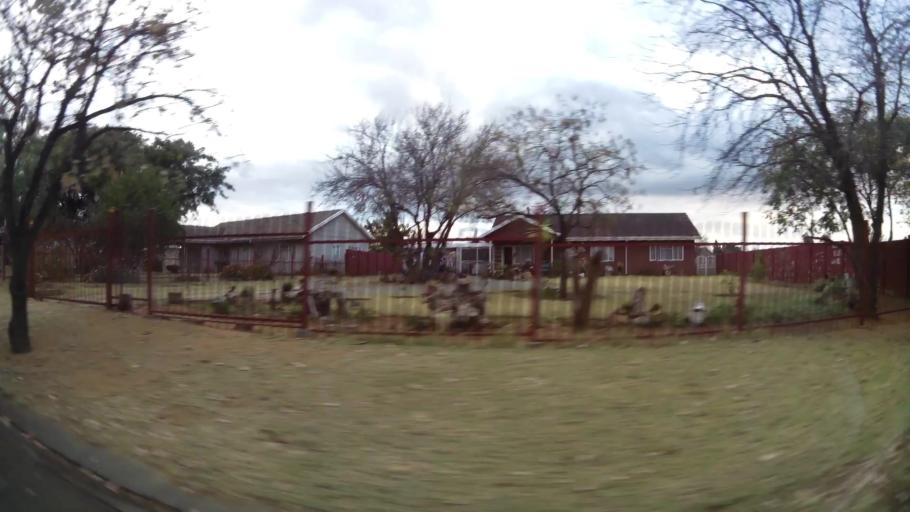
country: ZA
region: Orange Free State
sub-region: Lejweleputswa District Municipality
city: Welkom
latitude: -27.9473
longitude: 26.7246
